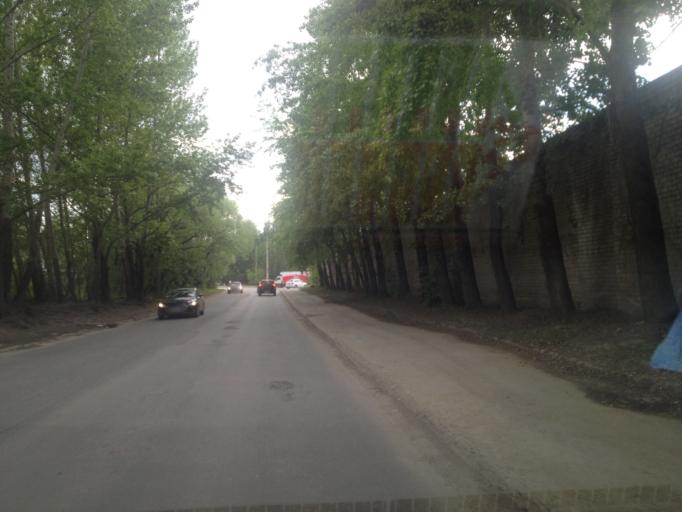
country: RU
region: Sverdlovsk
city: Sovkhoznyy
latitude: 56.7677
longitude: 60.5517
